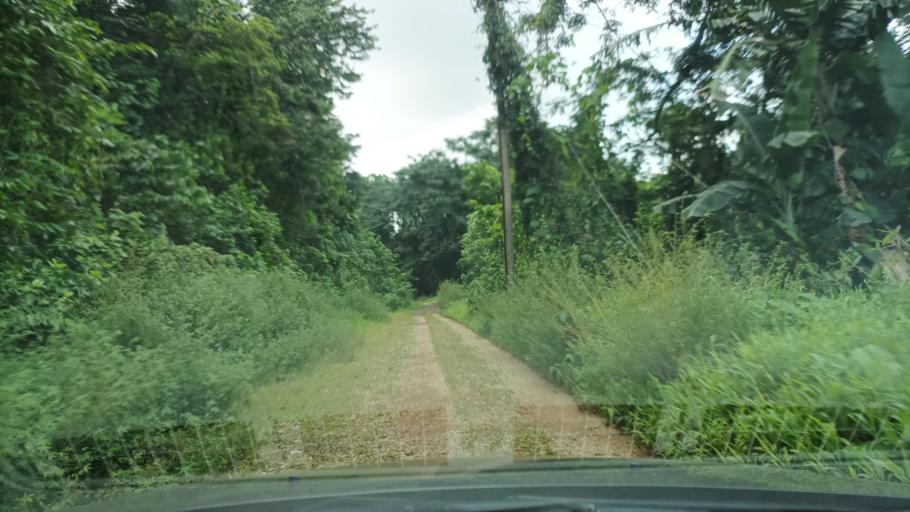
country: FM
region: Kosrae
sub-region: Utwe Municipality
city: Utwe
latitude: 5.2759
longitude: 162.9544
